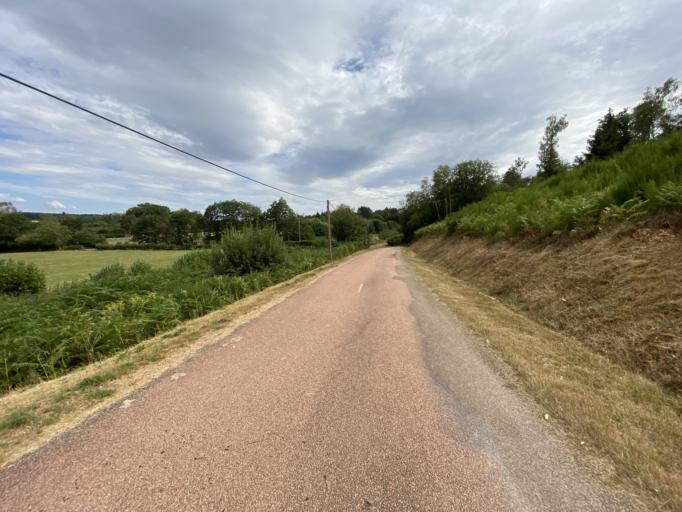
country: FR
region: Bourgogne
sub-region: Departement de la Cote-d'Or
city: Saulieu
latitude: 47.2758
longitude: 4.1384
